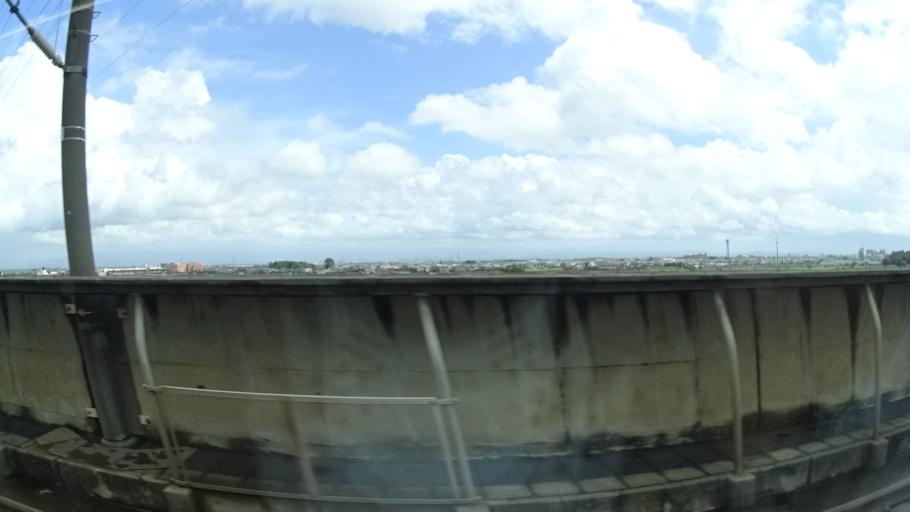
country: JP
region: Saitama
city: Honjo
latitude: 36.2356
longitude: 139.1452
